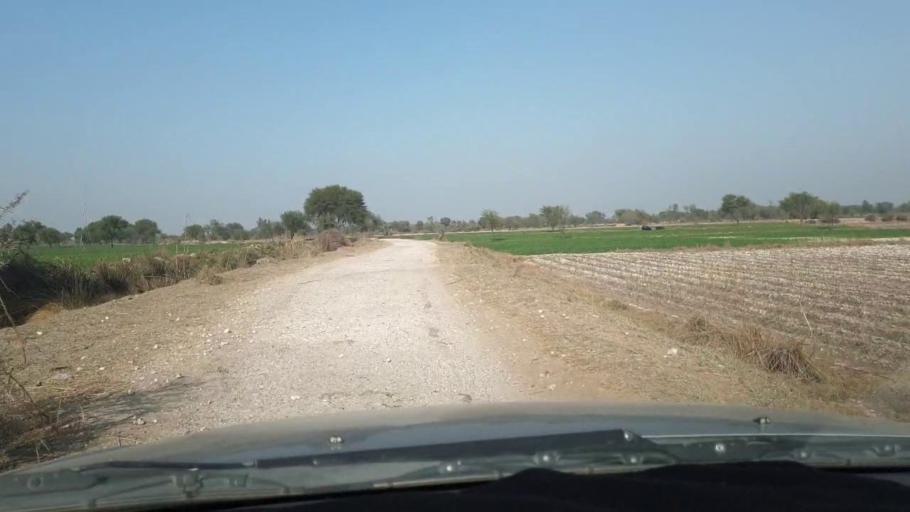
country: PK
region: Sindh
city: Mirpur Mathelo
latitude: 27.9298
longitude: 69.5631
